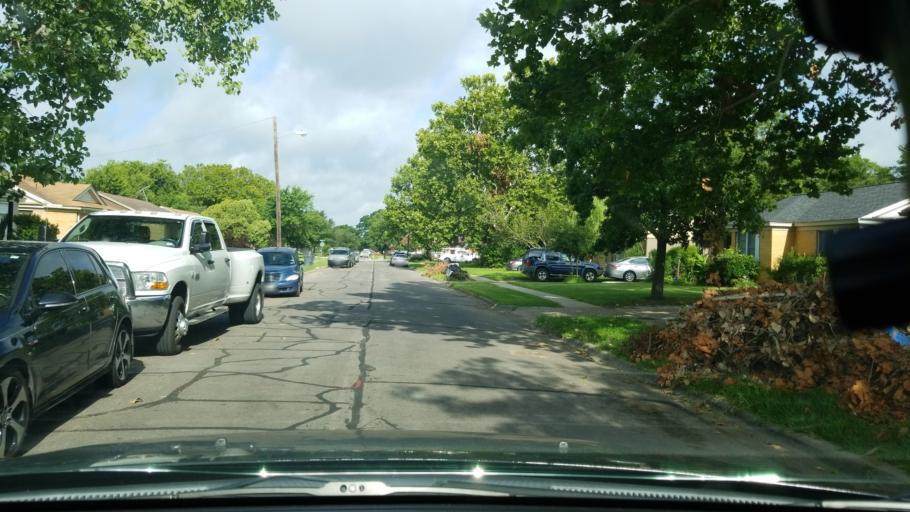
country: US
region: Texas
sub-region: Dallas County
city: Mesquite
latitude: 32.8189
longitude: -96.6670
